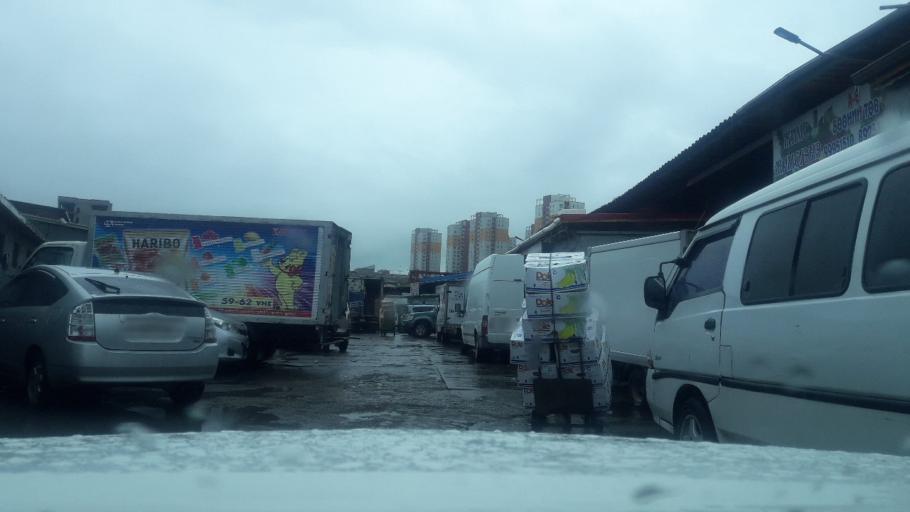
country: MN
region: Ulaanbaatar
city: Ulaanbaatar
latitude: 47.9085
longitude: 106.8912
